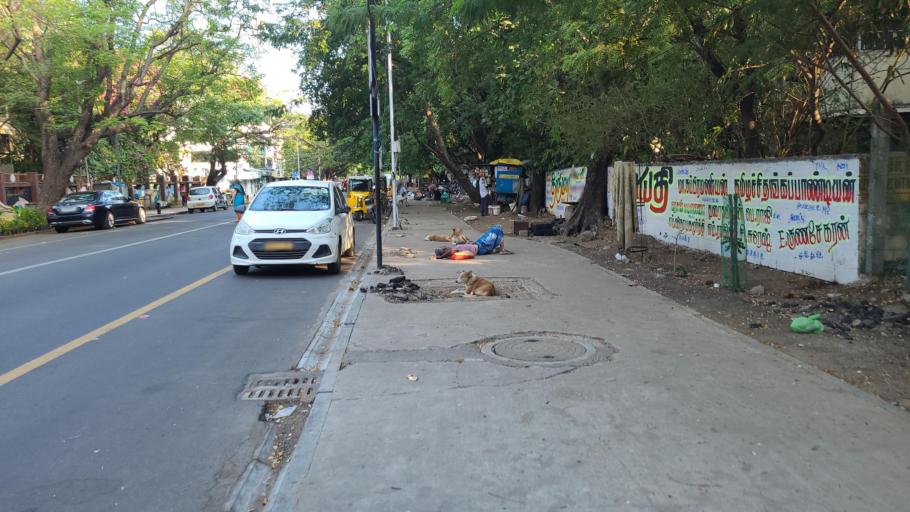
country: IN
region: Tamil Nadu
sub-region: Chennai
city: Gandhi Nagar
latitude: 12.9993
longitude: 80.2670
